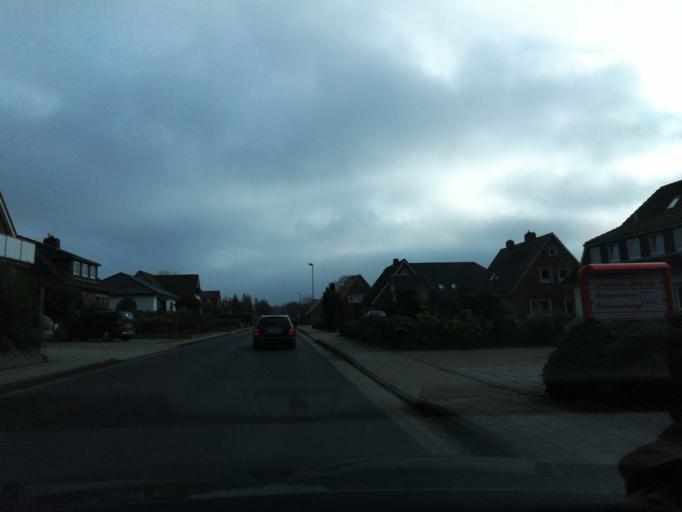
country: DE
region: Lower Saxony
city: Werdum
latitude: 53.6911
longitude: 7.8121
